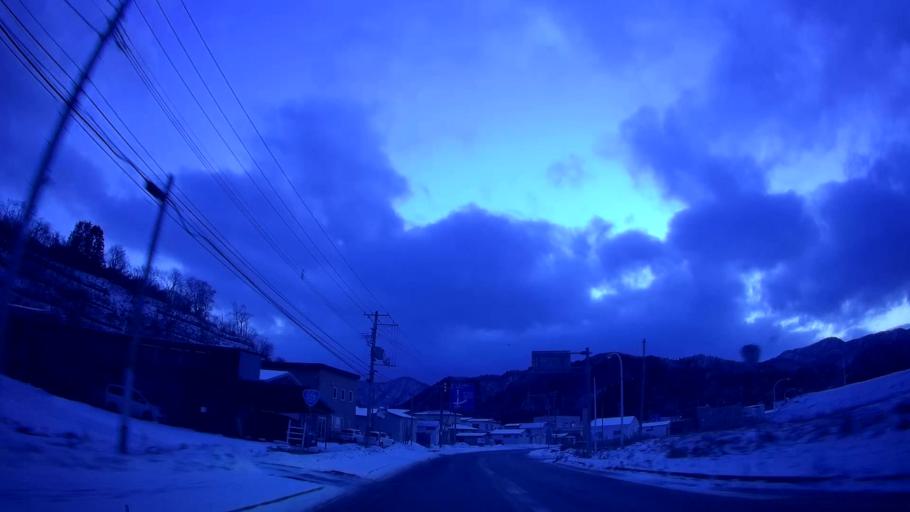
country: JP
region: Hokkaido
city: Hakodate
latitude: 41.8920
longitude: 141.0237
